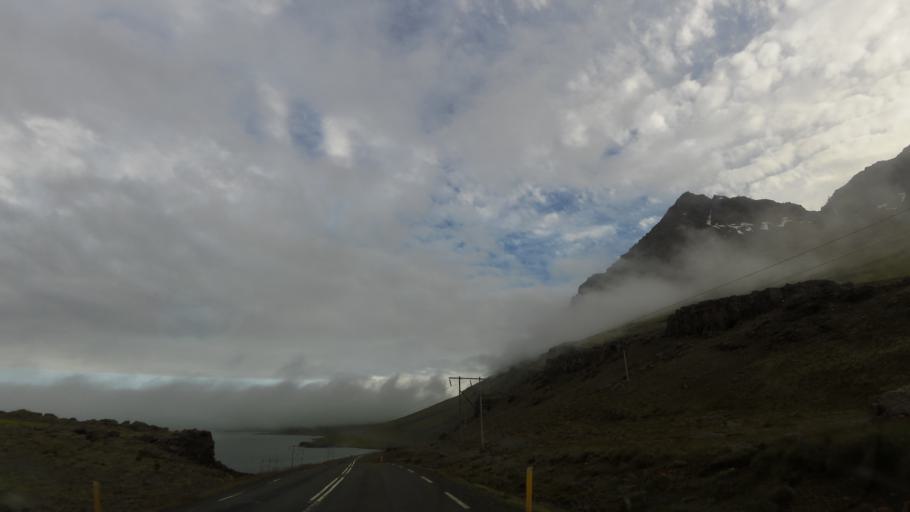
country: IS
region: East
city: Reydarfjoerdur
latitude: 64.7135
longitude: -14.4012
